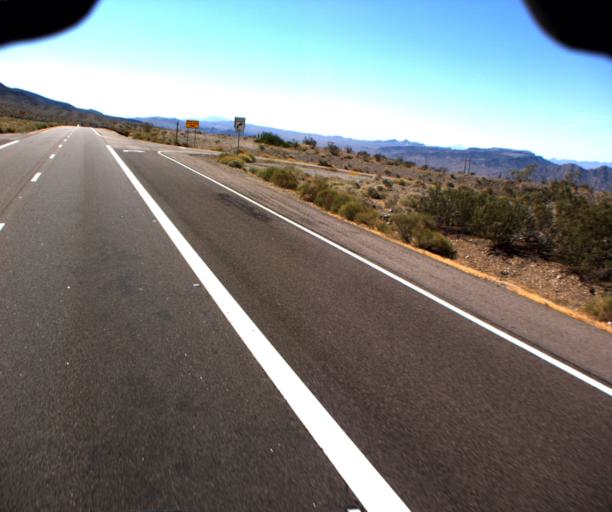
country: US
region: Nevada
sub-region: Clark County
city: Boulder City
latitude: 35.9354
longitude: -114.6382
